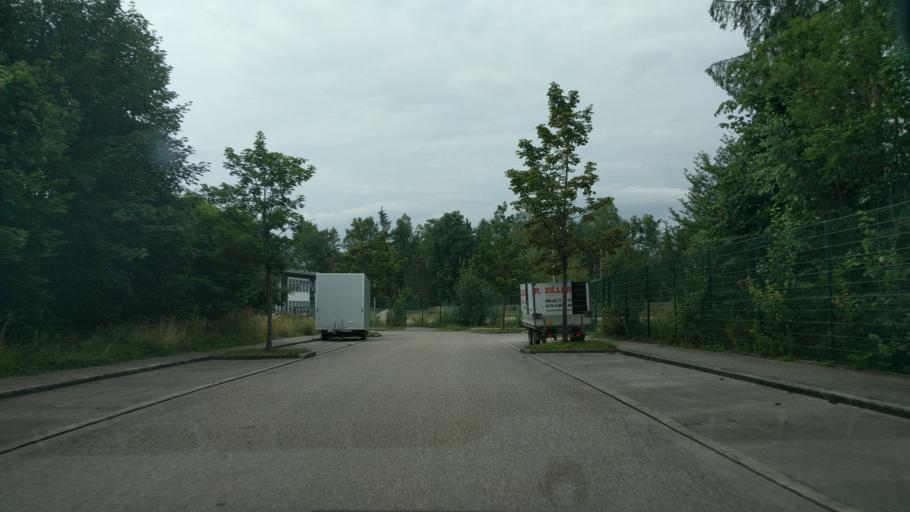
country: DE
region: Bavaria
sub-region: Upper Bavaria
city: Pullach im Isartal
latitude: 48.0629
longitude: 11.5548
